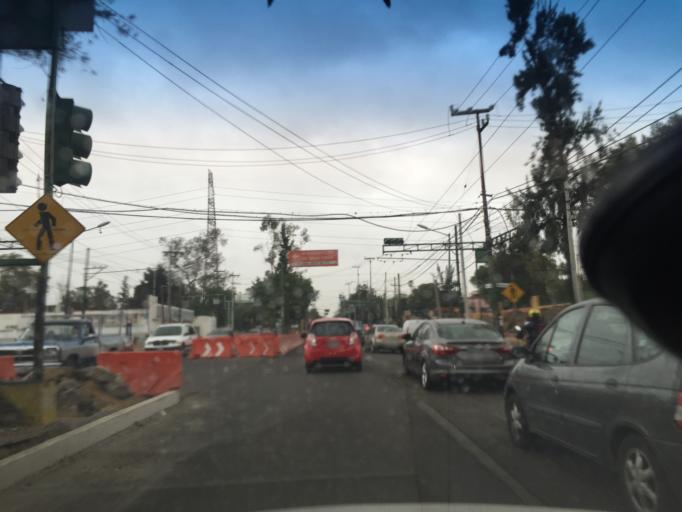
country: MX
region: Mexico City
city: Gustavo A. Madero
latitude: 19.4761
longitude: -99.0904
